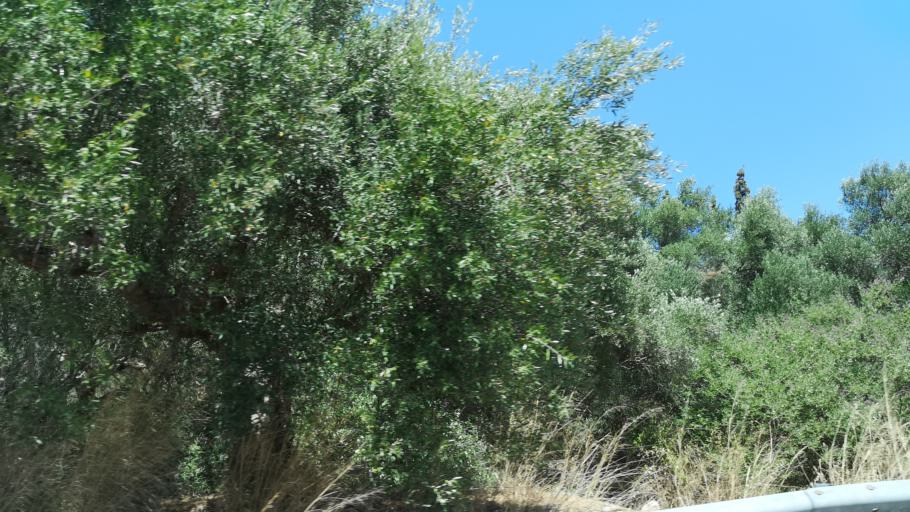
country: GR
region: Crete
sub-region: Nomos Lasithiou
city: Neapoli
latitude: 35.2422
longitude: 25.6444
